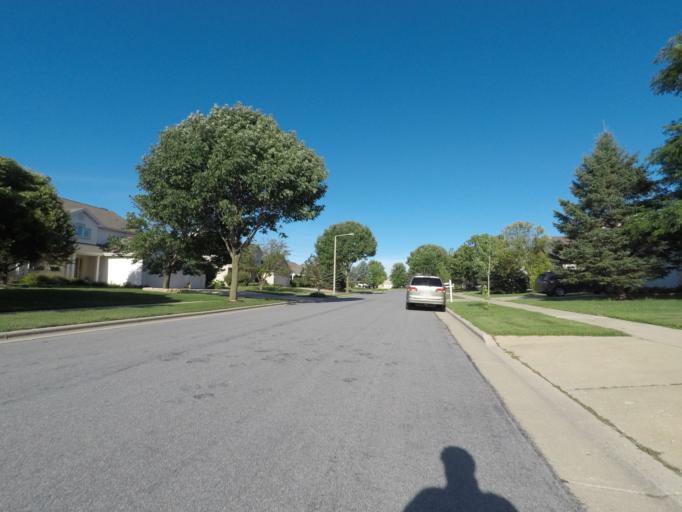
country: US
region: Wisconsin
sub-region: Dane County
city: Middleton
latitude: 43.0690
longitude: -89.5297
